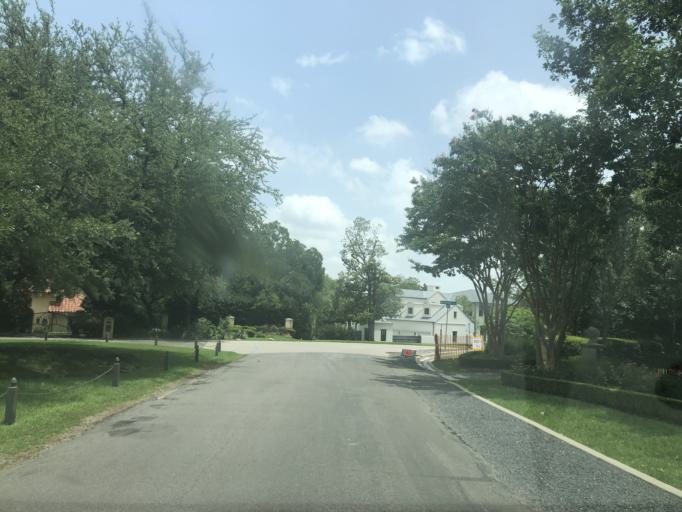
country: US
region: Texas
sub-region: Dallas County
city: University Park
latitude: 32.8754
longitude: -96.8329
